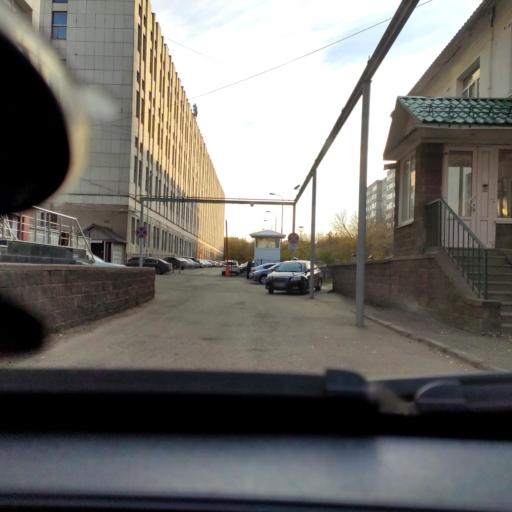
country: RU
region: Bashkortostan
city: Ufa
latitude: 54.7503
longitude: 56.0078
